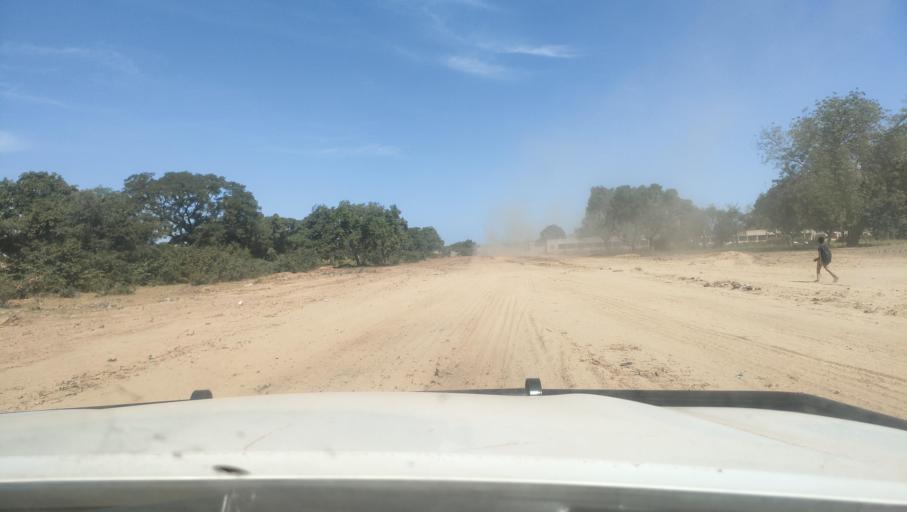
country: BF
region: Est
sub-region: Province du Gourma
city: Fada N'gourma
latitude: 12.0695
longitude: 0.3340
